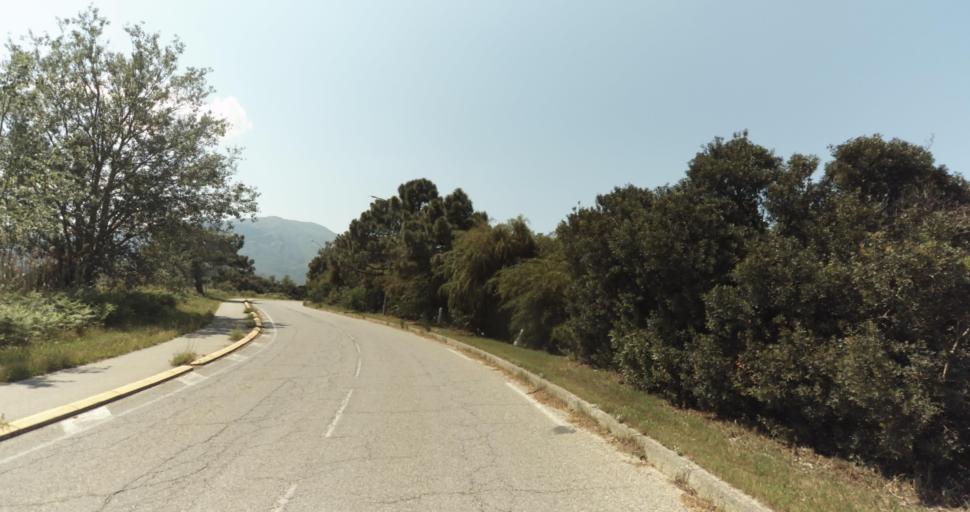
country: FR
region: Corsica
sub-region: Departement de la Haute-Corse
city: Biguglia
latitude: 42.6429
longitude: 9.4590
